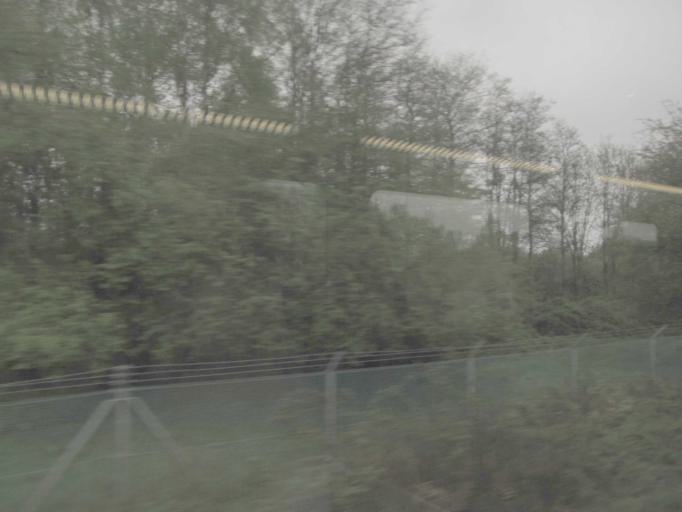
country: GB
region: England
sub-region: Surrey
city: Frimley
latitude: 51.3171
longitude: -0.7626
